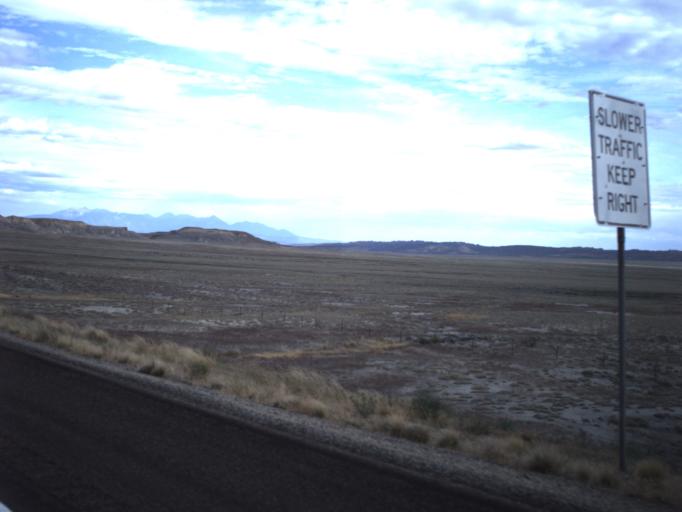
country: US
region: Utah
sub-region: Grand County
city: Moab
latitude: 38.9534
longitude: -109.7018
